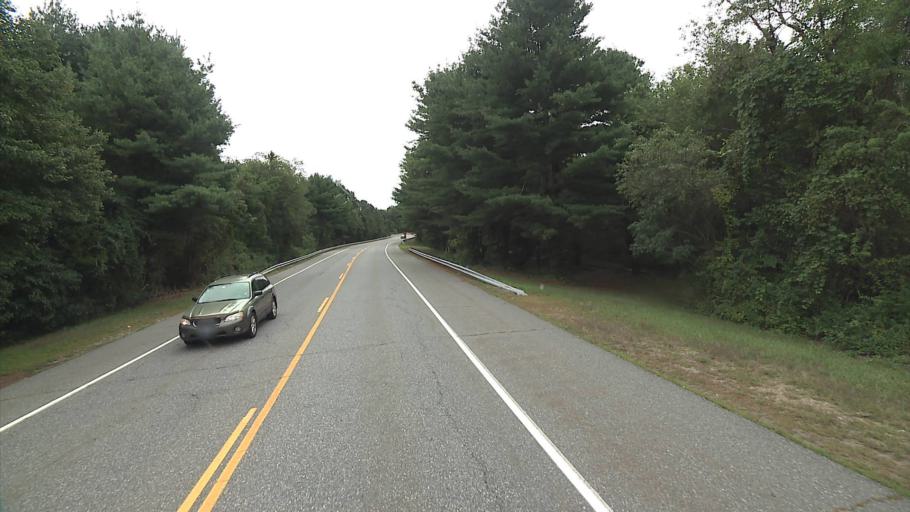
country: US
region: Connecticut
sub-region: Middlesex County
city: Old Saybrook Center
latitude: 41.3081
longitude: -72.3317
